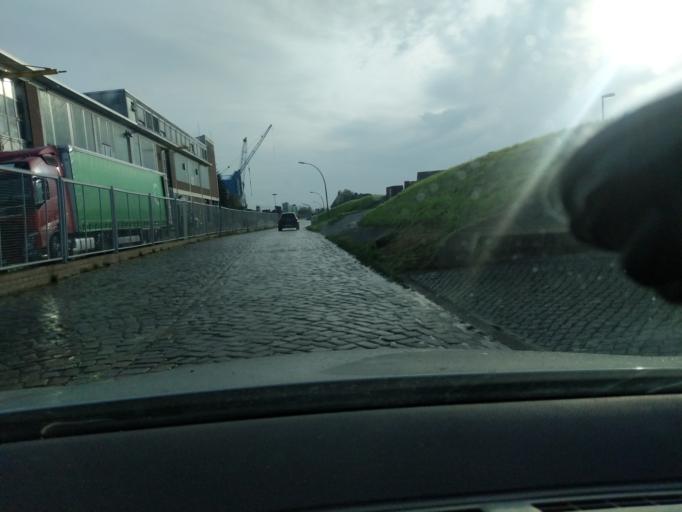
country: DE
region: Lower Saxony
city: Neu Wulmstorf
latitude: 53.5318
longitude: 9.7847
